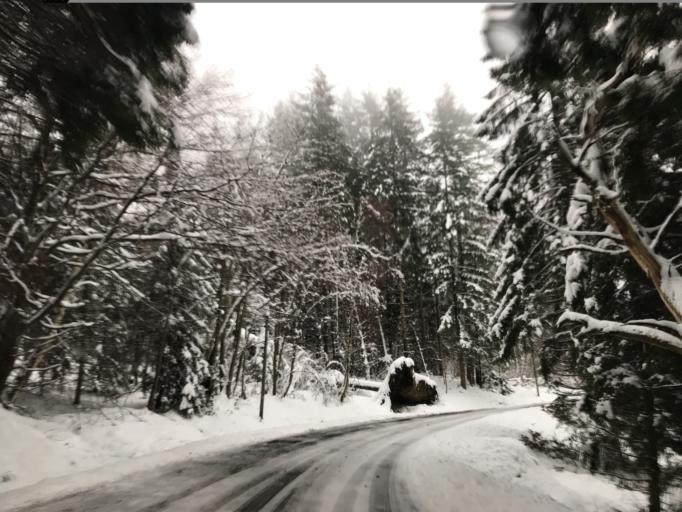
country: FR
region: Rhone-Alpes
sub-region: Departement de la Loire
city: Noiretable
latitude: 45.7417
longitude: 3.6798
